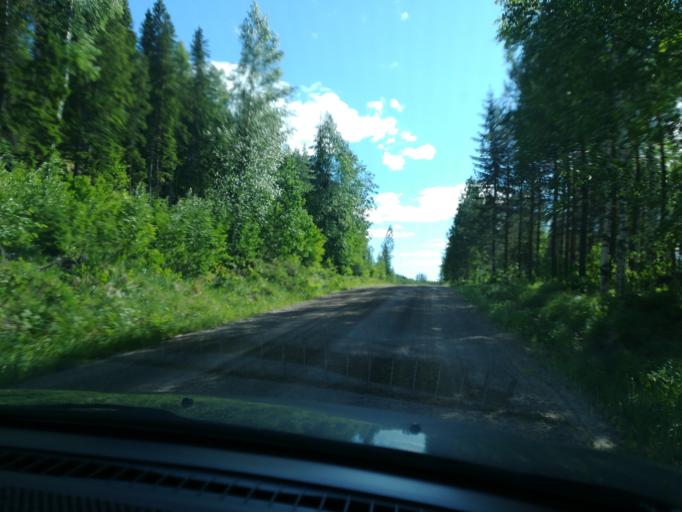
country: FI
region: Southern Savonia
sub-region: Mikkeli
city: Puumala
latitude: 61.6528
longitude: 28.1086
